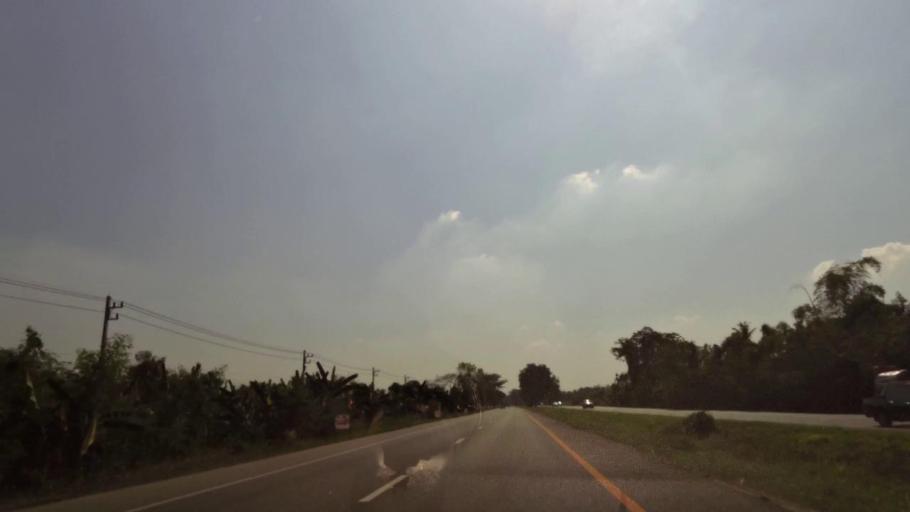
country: TH
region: Phichit
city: Bueng Na Rang
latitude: 16.2387
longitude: 100.1254
